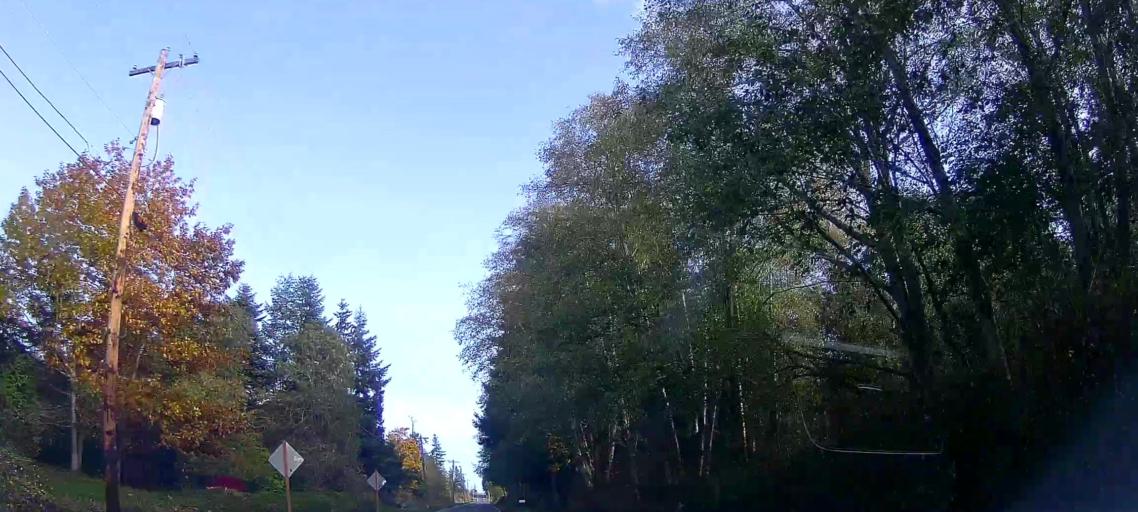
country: US
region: Washington
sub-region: Snohomish County
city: Stanwood
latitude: 48.2546
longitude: -122.4641
